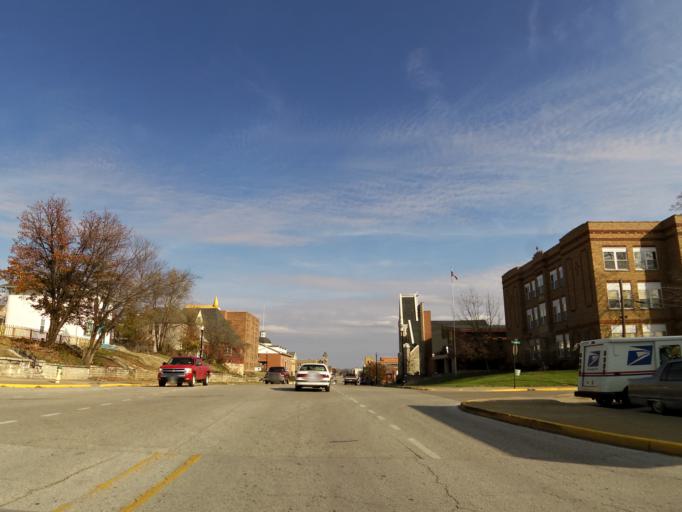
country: US
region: Missouri
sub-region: Marion County
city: Hannibal
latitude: 39.7050
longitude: -91.3670
